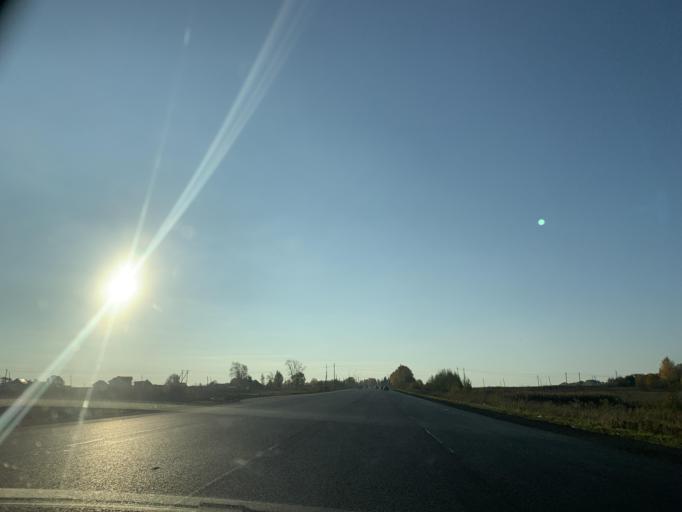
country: RU
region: Jaroslavl
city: Konstantinovskiy
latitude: 57.7930
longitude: 39.6046
